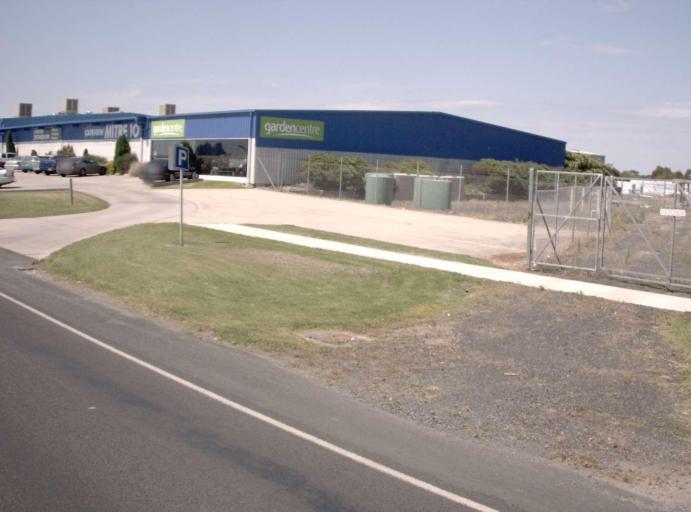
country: AU
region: Victoria
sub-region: Bass Coast
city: North Wonthaggi
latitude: -38.6173
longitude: 145.5993
